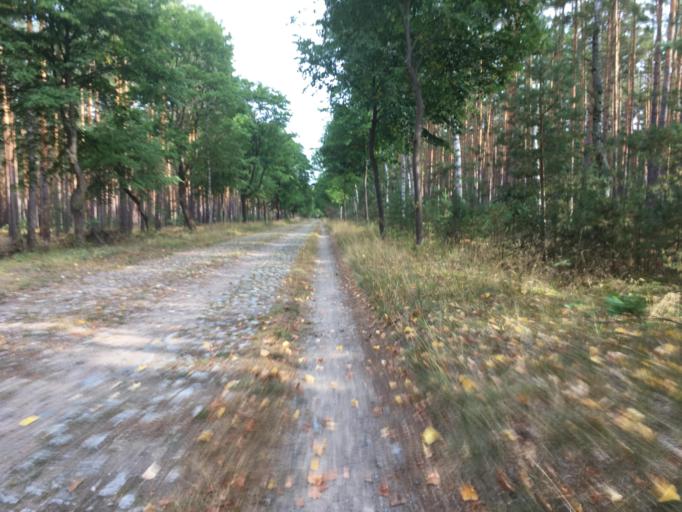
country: DE
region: Brandenburg
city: Marienwerder
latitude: 52.9268
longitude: 13.5196
